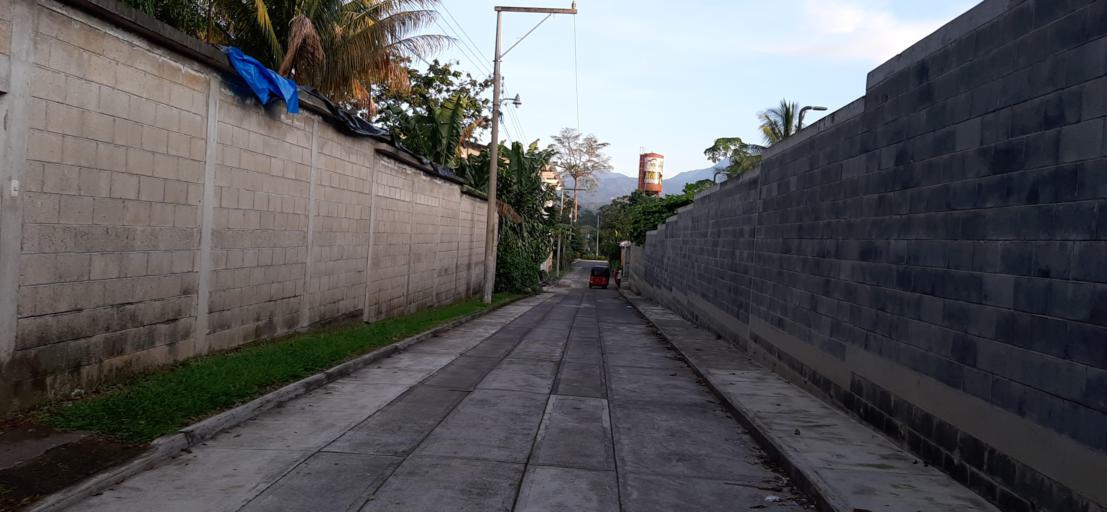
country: GT
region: Retalhuleu
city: San Felipe
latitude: 14.6233
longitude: -91.6016
